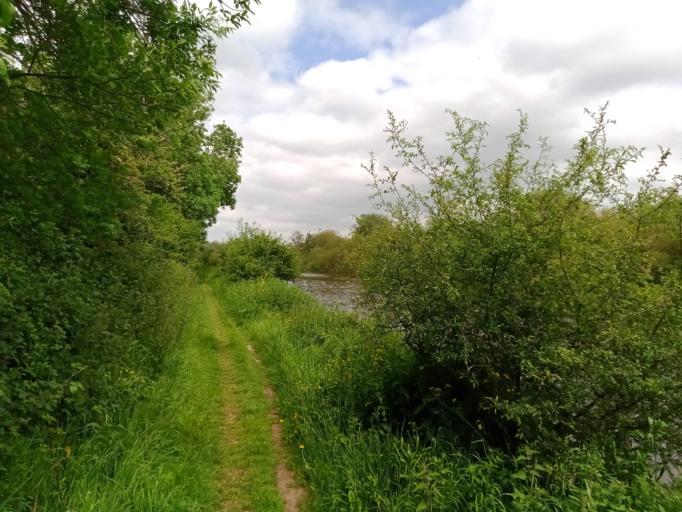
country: IE
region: Leinster
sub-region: County Carlow
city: Carlow
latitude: 52.7910
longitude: -6.9606
